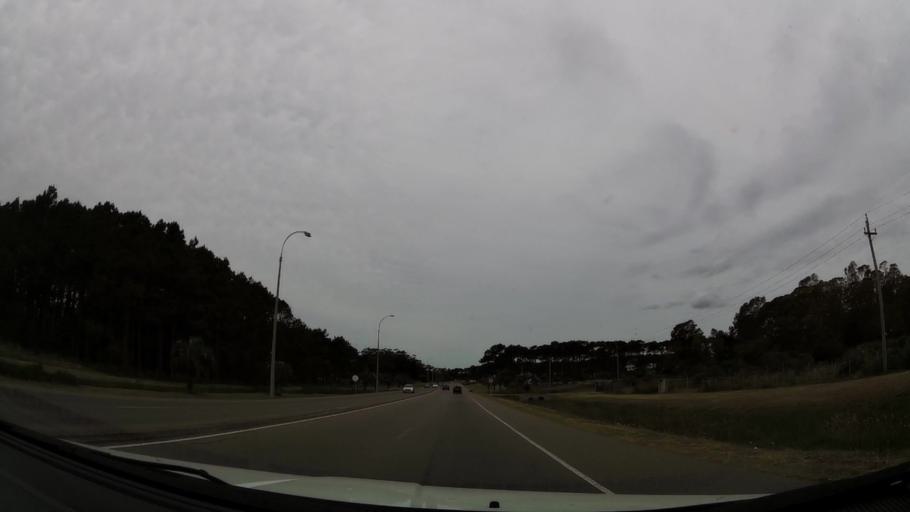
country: UY
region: Maldonado
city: Maldonado
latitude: -34.9048
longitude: -55.0313
